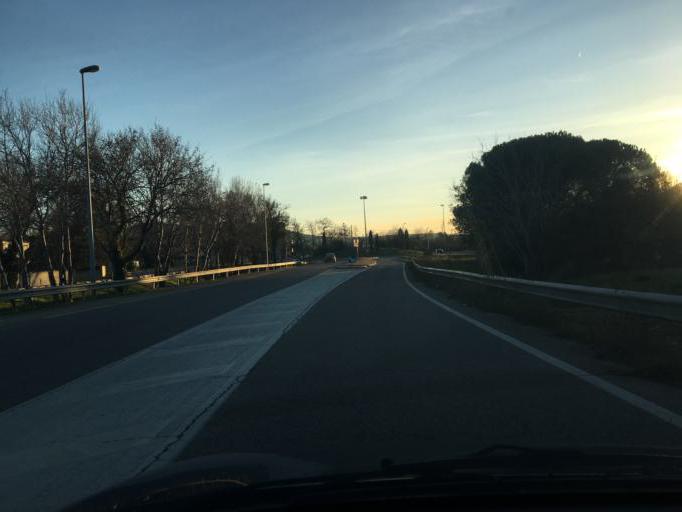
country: FR
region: Provence-Alpes-Cote d'Azur
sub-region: Departement des Bouches-du-Rhone
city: Mallemort
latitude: 43.7353
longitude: 5.1725
